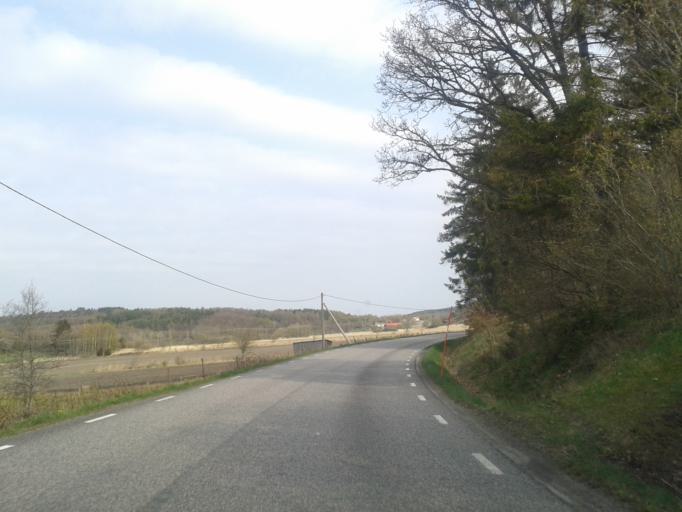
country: SE
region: Vaestra Goetaland
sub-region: Kungalvs Kommun
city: Kode
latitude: 57.8986
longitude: 11.8030
